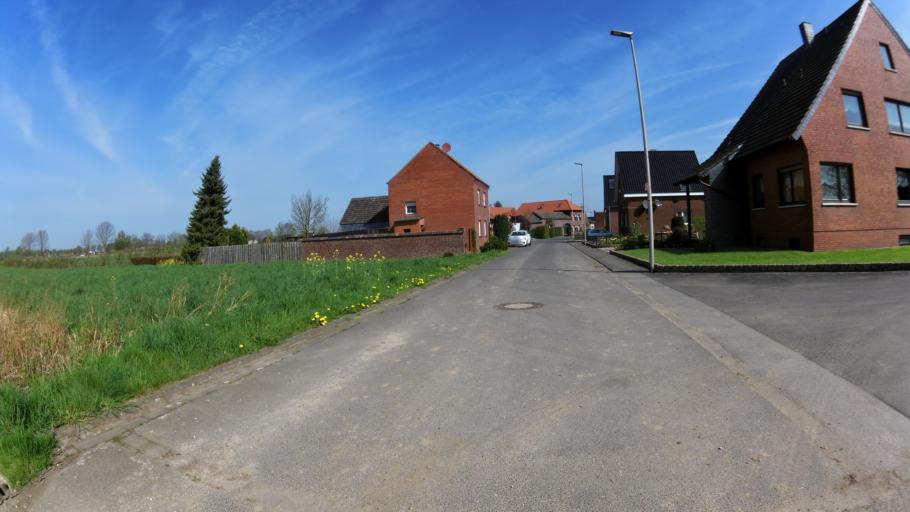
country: DE
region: North Rhine-Westphalia
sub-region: Regierungsbezirk Koln
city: Gangelt
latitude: 51.0001
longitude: 6.0345
